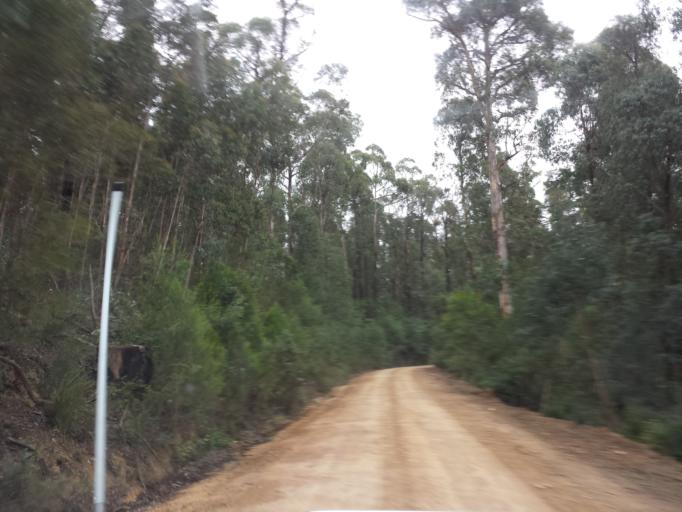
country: AU
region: Victoria
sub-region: Latrobe
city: Traralgon
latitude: -37.9881
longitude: 146.4408
